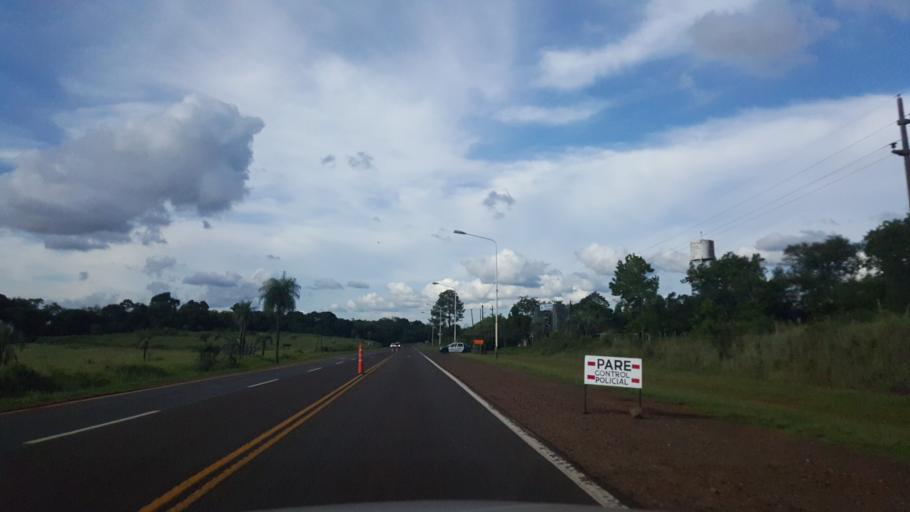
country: AR
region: Misiones
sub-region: Departamento de Candelaria
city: Loreto
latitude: -27.3375
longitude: -55.5446
